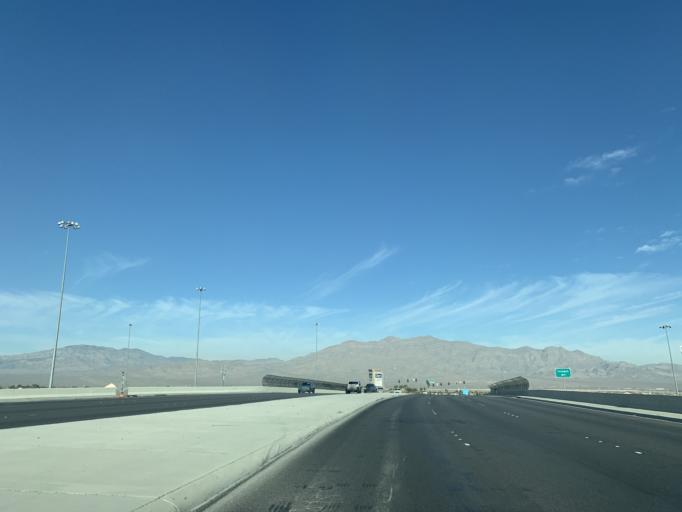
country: US
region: Nevada
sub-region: Clark County
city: Summerlin South
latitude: 36.2975
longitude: -115.2867
